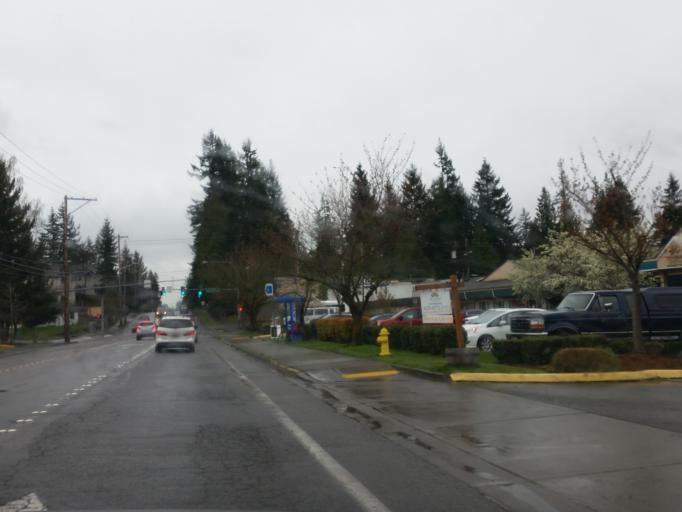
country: US
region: Washington
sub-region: Snohomish County
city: Lynnwood
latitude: 47.8175
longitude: -122.3155
